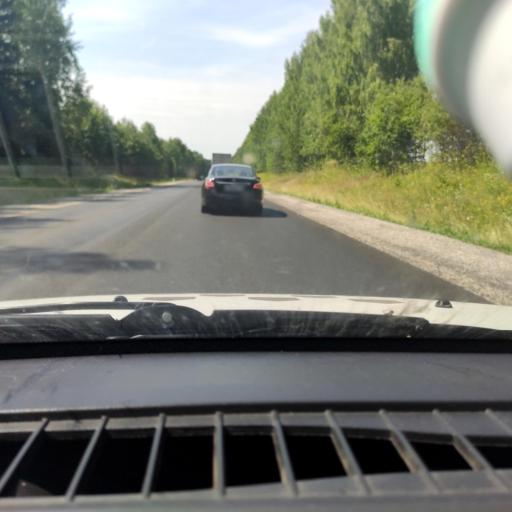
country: RU
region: Perm
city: Zyukayka
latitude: 58.2952
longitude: 54.7868
